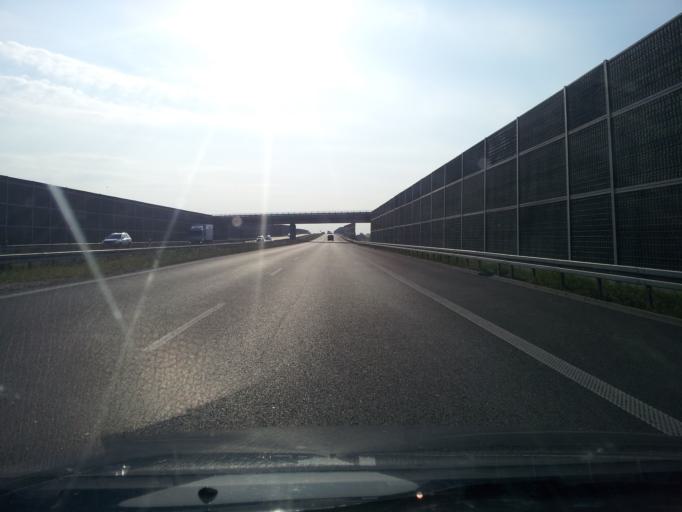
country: PL
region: Masovian Voivodeship
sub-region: Powiat zyrardowski
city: Wiskitki
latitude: 52.0974
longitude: 20.4011
